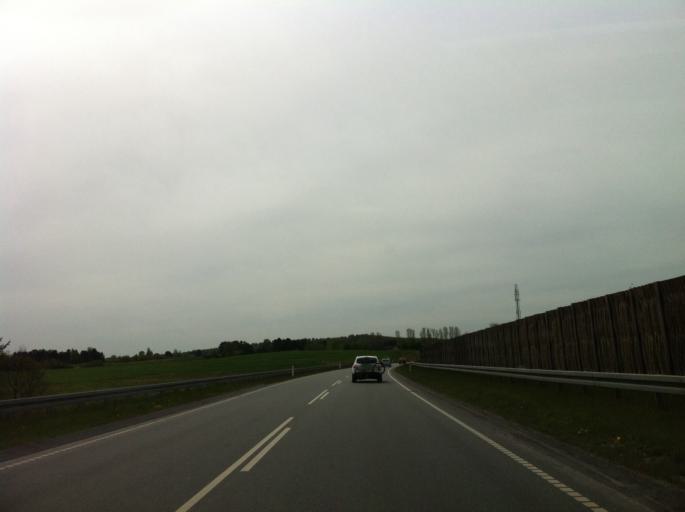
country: DK
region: Capital Region
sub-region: Frederikssund Kommune
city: Slangerup
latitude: 55.8858
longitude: 12.2053
